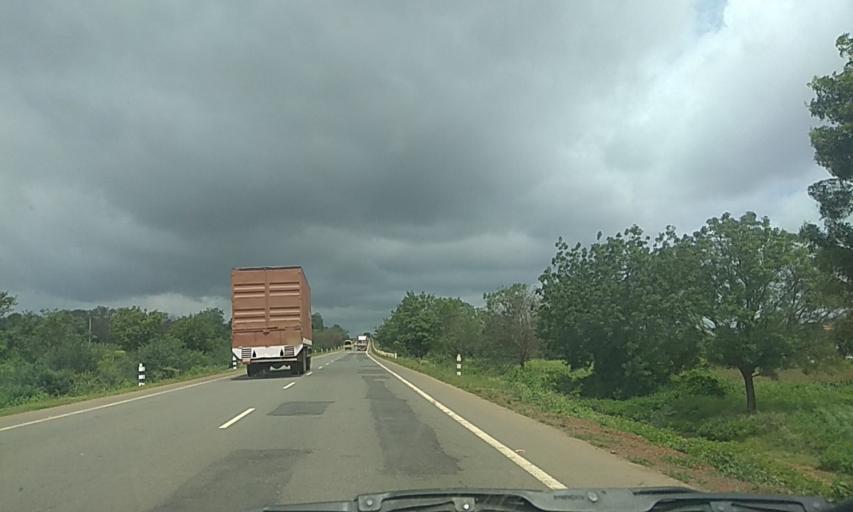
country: IN
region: Karnataka
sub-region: Dharwad
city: Hubli
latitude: 15.3397
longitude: 75.0850
